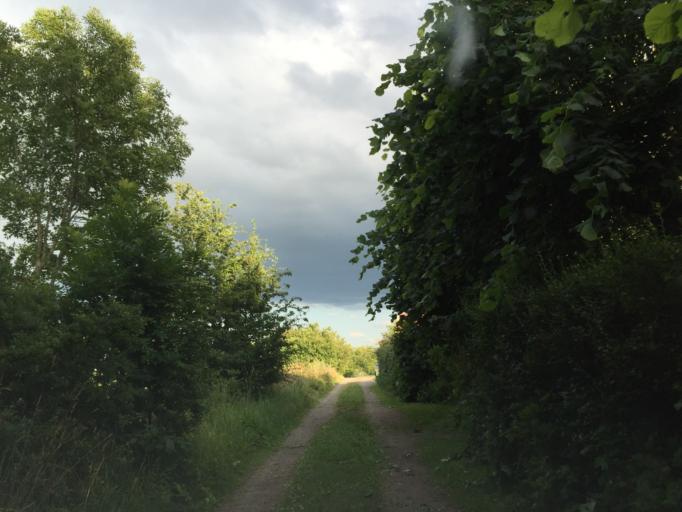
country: SE
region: OEstergoetland
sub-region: Vadstena Kommun
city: Vadstena
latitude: 58.4667
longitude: 14.8417
